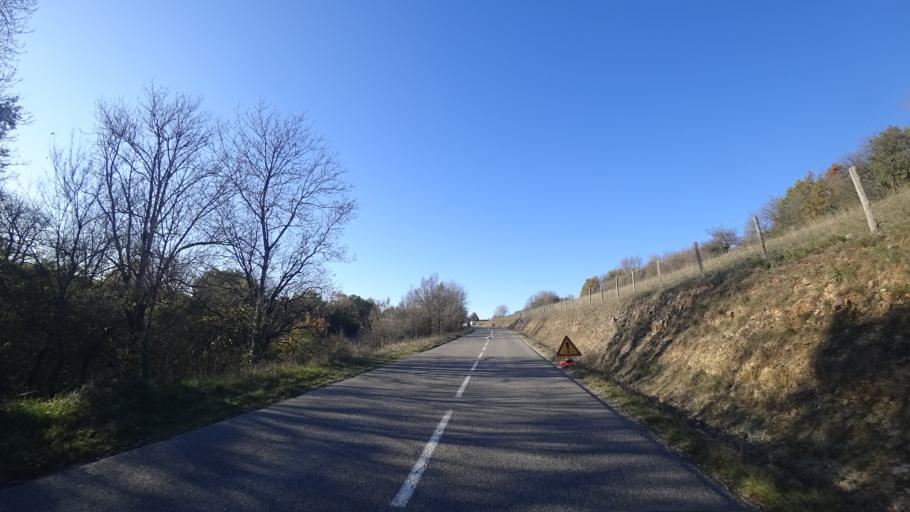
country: FR
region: Midi-Pyrenees
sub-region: Departement de l'Aveyron
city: Rodez
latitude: 44.3802
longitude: 2.5575
